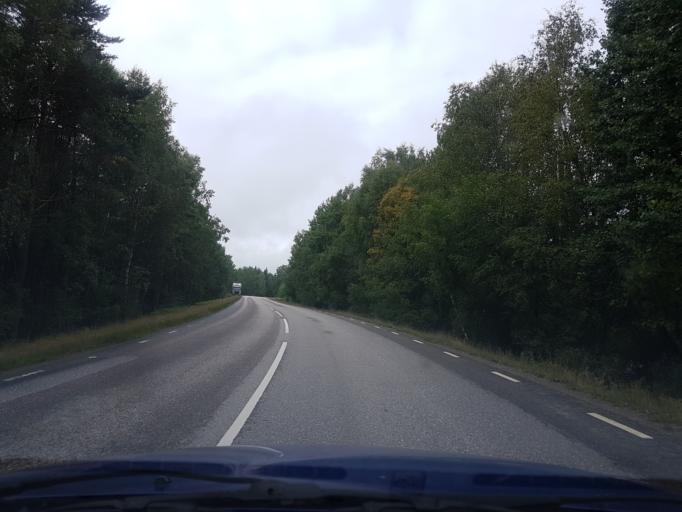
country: SE
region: Vaestra Goetaland
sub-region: Ale Kommun
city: Salanda
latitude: 57.9477
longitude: 12.2095
